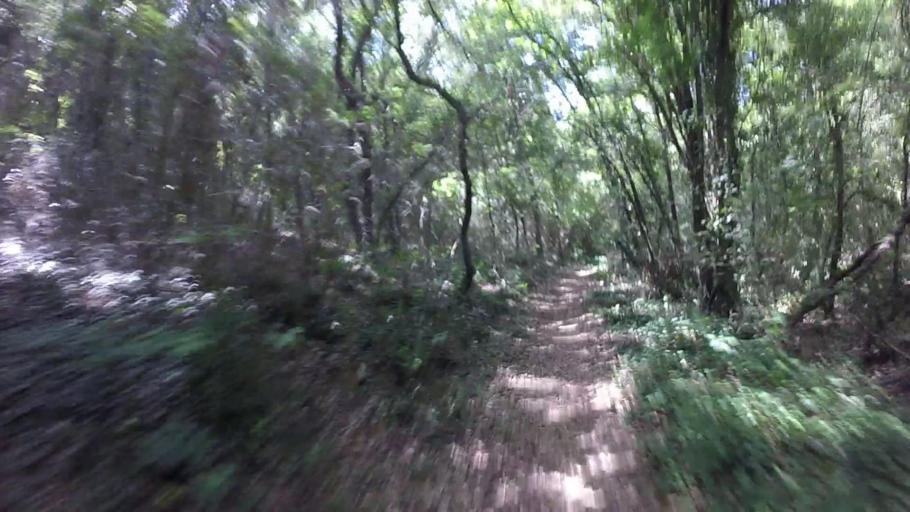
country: FR
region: Provence-Alpes-Cote d'Azur
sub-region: Departement des Alpes-Maritimes
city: Mougins
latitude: 43.6160
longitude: 7.0255
